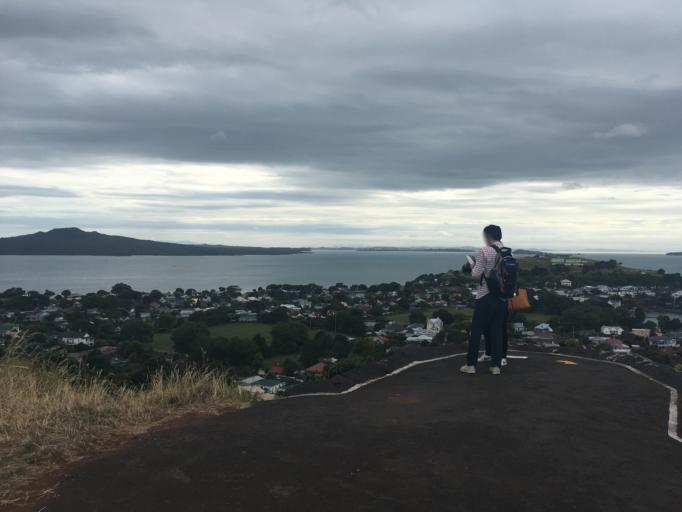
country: NZ
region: Auckland
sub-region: Auckland
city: Auckland
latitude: -36.8269
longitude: 174.7999
